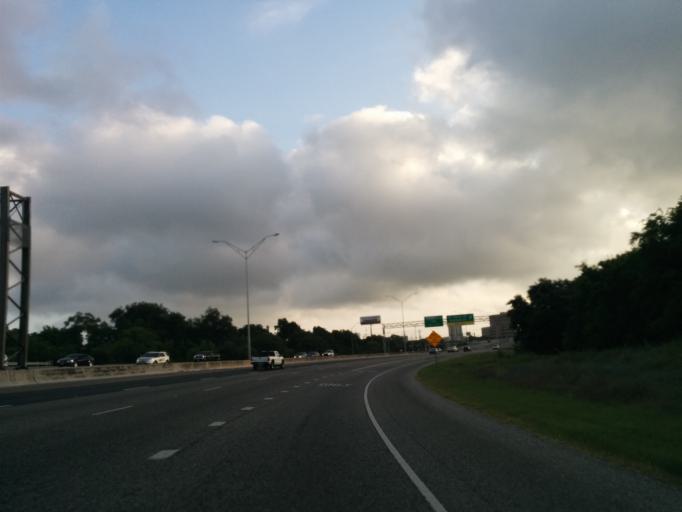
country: US
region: Texas
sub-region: Bexar County
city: San Antonio
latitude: 29.4505
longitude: -98.4837
